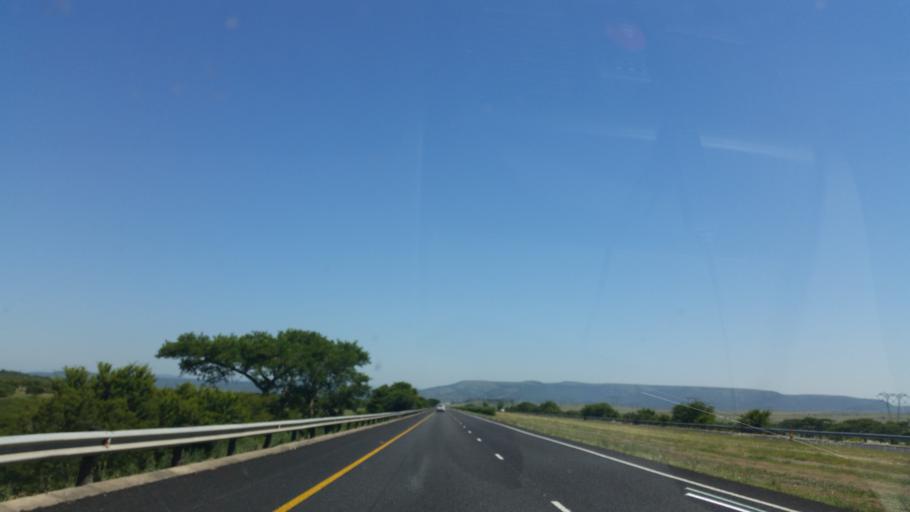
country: ZA
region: KwaZulu-Natal
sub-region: uThukela District Municipality
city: Estcourt
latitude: -28.8208
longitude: 29.6977
